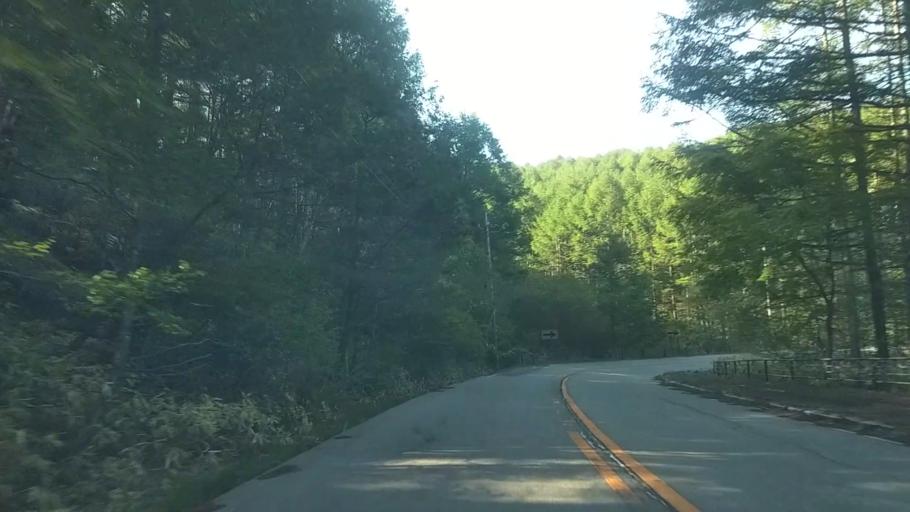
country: JP
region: Yamanashi
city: Nirasaki
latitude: 35.9126
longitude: 138.4009
